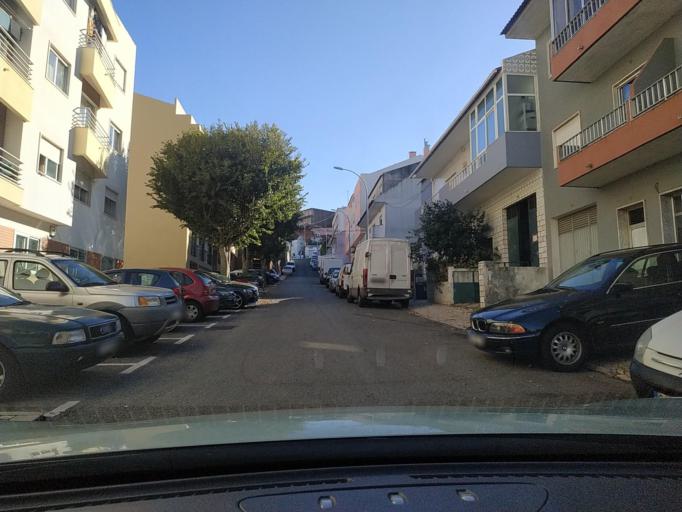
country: PT
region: Lisbon
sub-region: Amadora
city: Amadora
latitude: 38.7682
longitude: -9.2199
